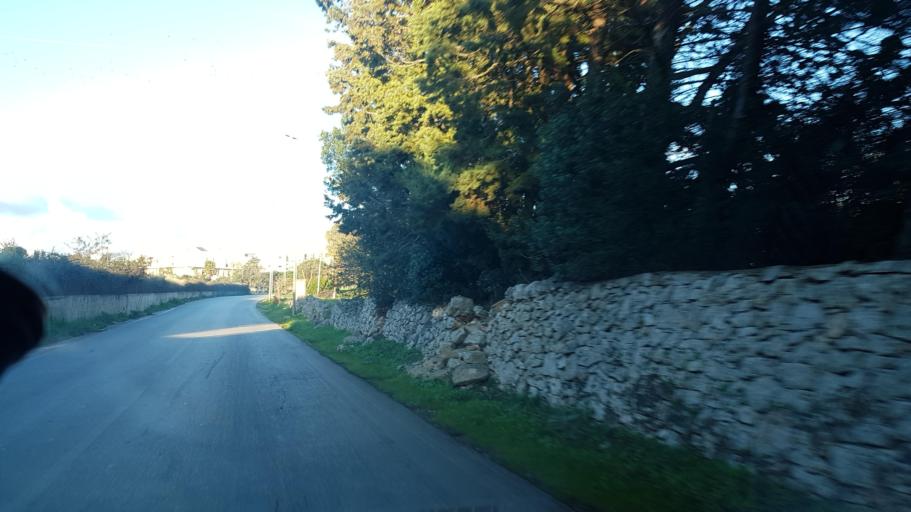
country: IT
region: Apulia
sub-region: Provincia di Brindisi
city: Ostuni
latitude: 40.7228
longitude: 17.5684
